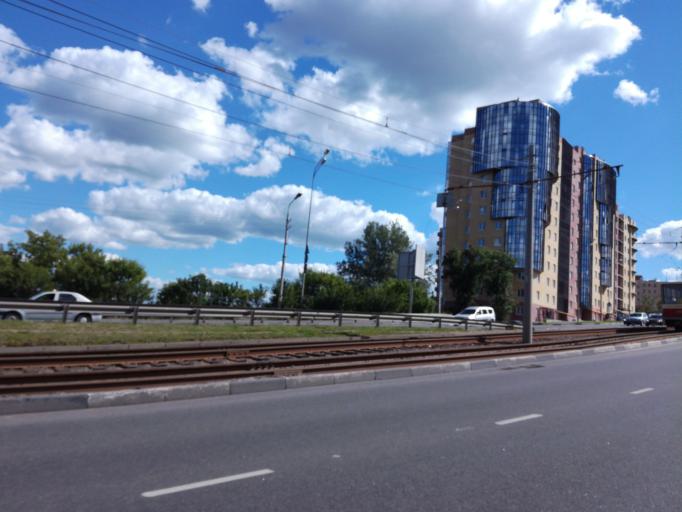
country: RU
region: Kursk
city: Kursk
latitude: 51.7553
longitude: 36.2041
